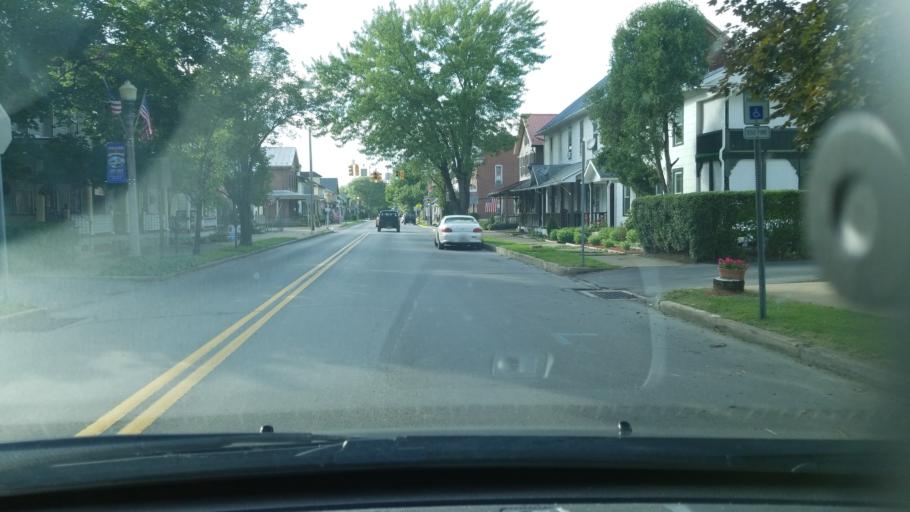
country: US
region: Pennsylvania
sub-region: Northumberland County
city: Watsontown
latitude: 41.0873
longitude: -76.8664
